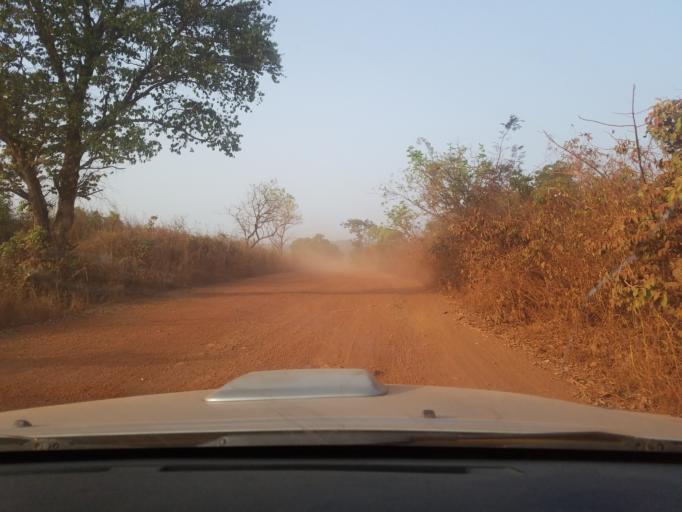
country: GN
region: Boke
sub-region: Gaoual Prefecture
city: Gaoual
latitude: 11.5061
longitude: -13.8596
